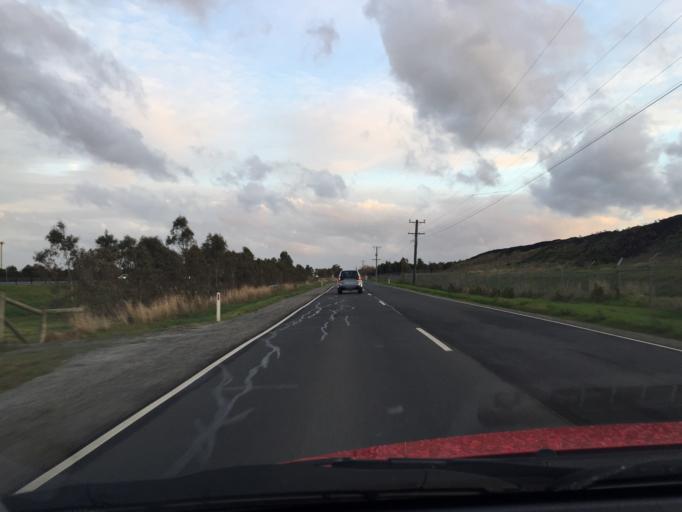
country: AU
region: Victoria
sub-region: Frankston
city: Sandhurst
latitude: -38.0442
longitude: 145.1862
